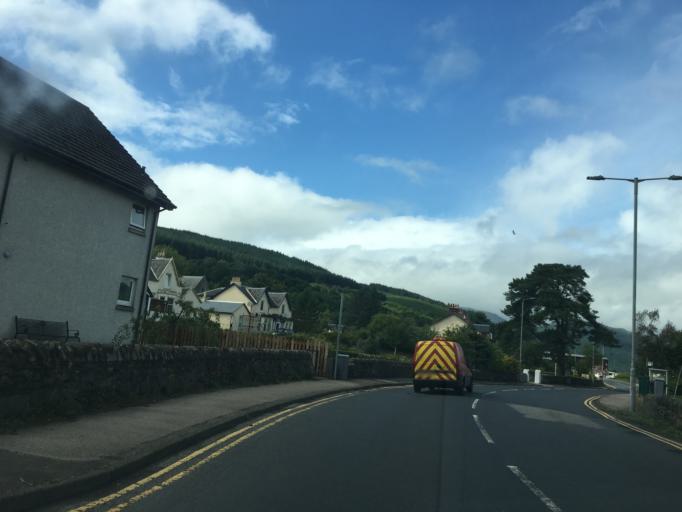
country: GB
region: Scotland
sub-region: Argyll and Bute
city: Dunoon
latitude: 55.9806
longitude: -4.9441
